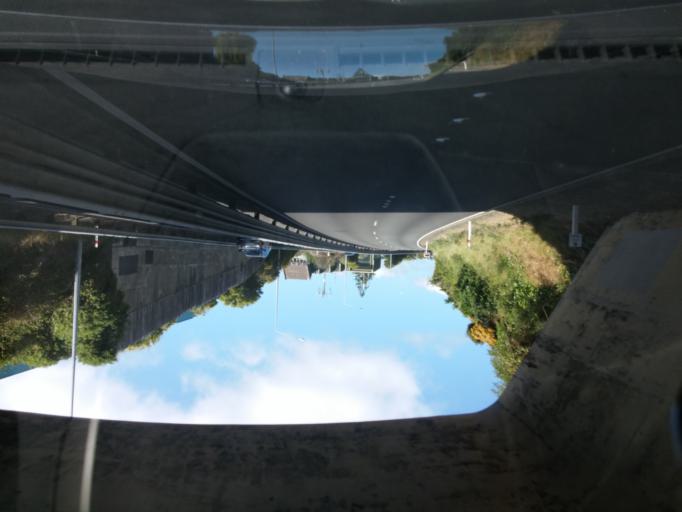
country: NZ
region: Wellington
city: Petone
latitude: -41.2213
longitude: 174.8092
